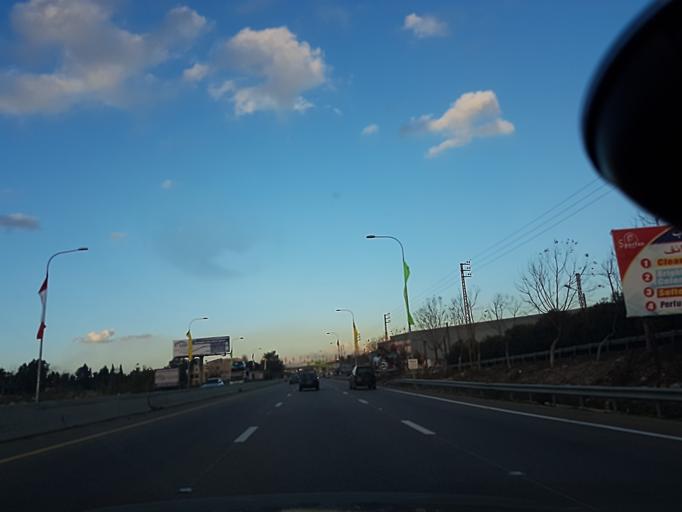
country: LB
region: Liban-Sud
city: Sidon
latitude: 33.5125
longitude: 35.3564
